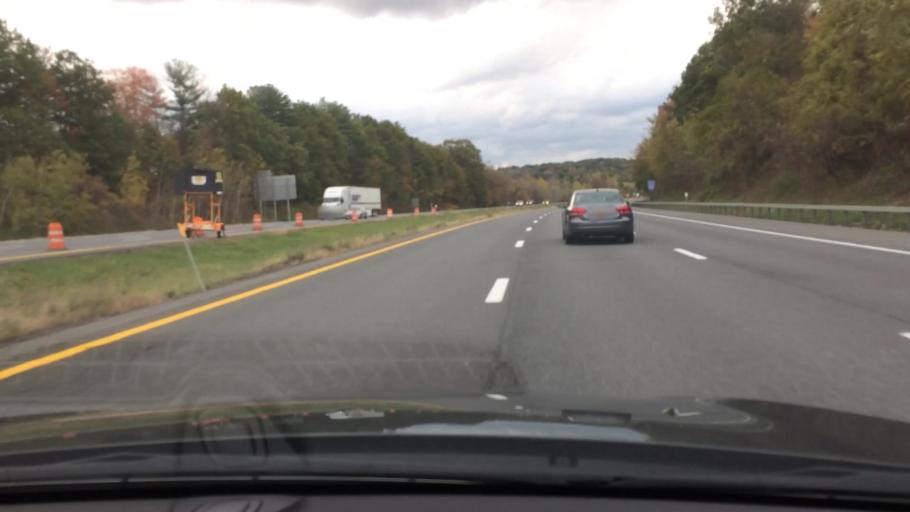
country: US
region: New York
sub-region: Rensselaer County
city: Hampton Manor
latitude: 42.6259
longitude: -73.6975
